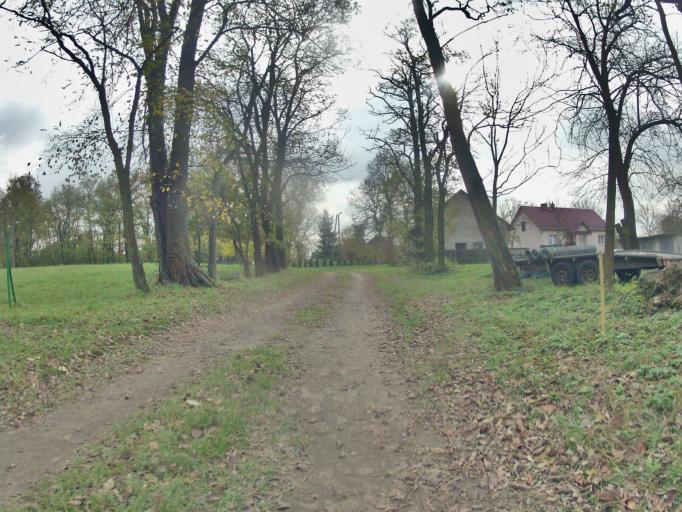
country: PL
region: Lesser Poland Voivodeship
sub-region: Powiat wielicki
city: Wegrzce Wielkie
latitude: 50.0496
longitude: 20.1140
